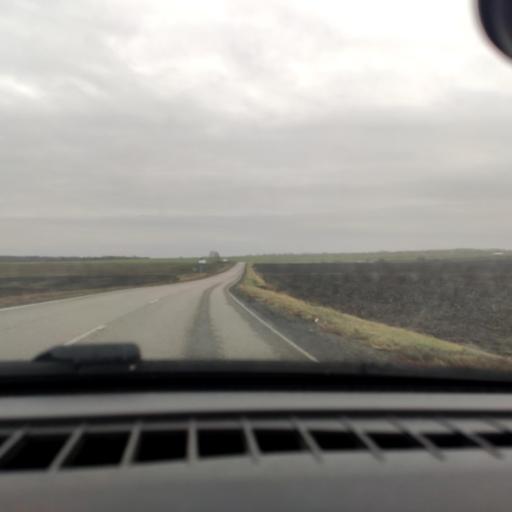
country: RU
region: Belgorod
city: Alekseyevka
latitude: 50.7761
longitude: 38.8321
